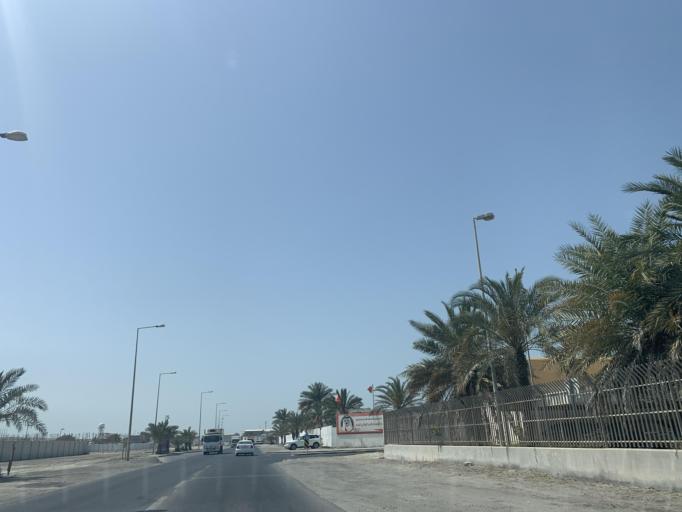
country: BH
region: Muharraq
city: Al Hadd
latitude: 26.2755
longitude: 50.6398
